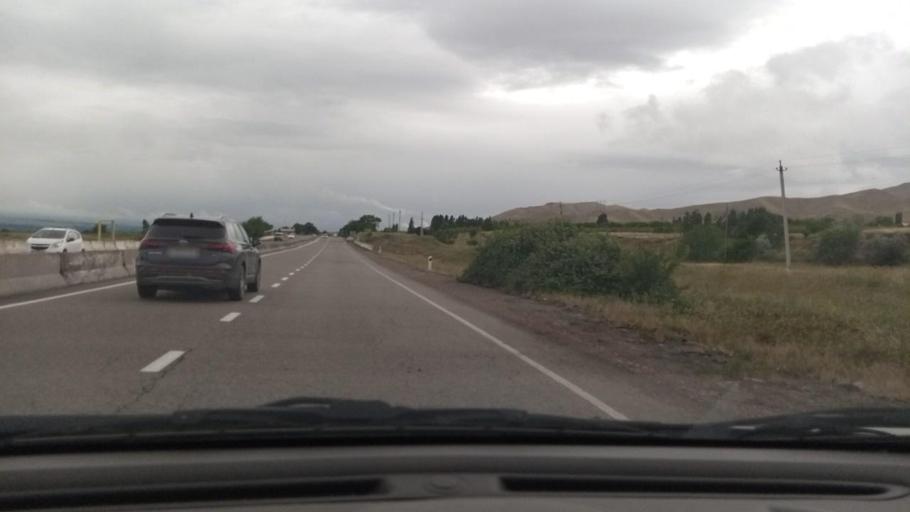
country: UZ
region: Toshkent
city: Angren
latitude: 40.9526
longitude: 69.9208
